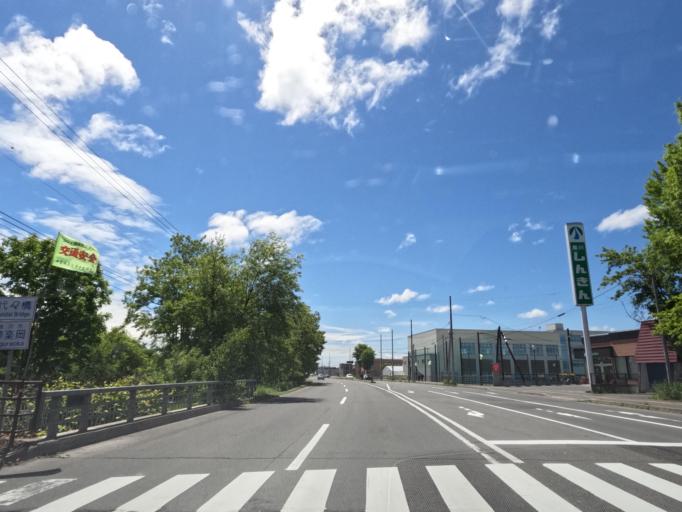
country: JP
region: Hokkaido
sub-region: Asahikawa-shi
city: Asahikawa
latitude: 43.7444
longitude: 142.3580
